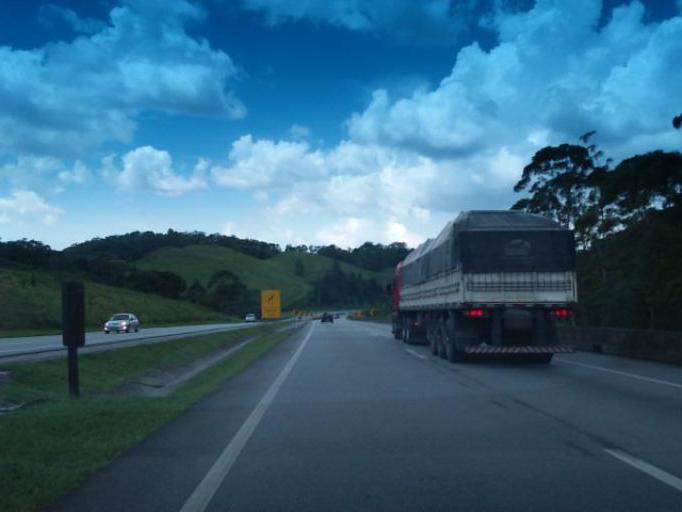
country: BR
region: Sao Paulo
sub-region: Juquitiba
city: Juquitiba
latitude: -23.9988
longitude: -47.1500
